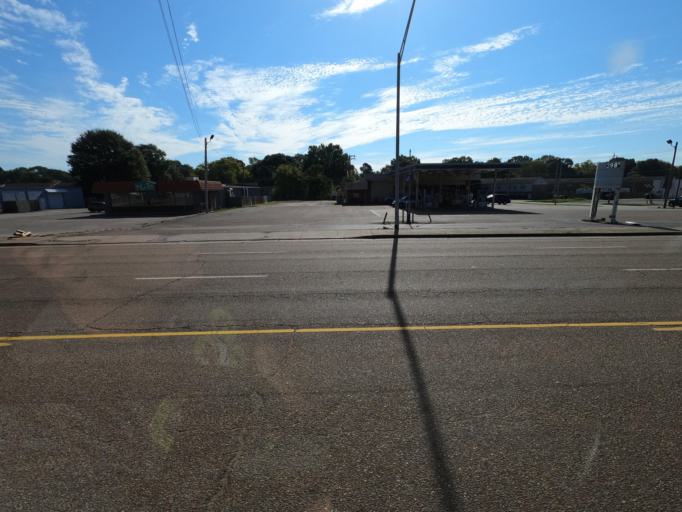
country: US
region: Tennessee
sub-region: Shelby County
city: Millington
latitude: 35.3385
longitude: -89.9130
